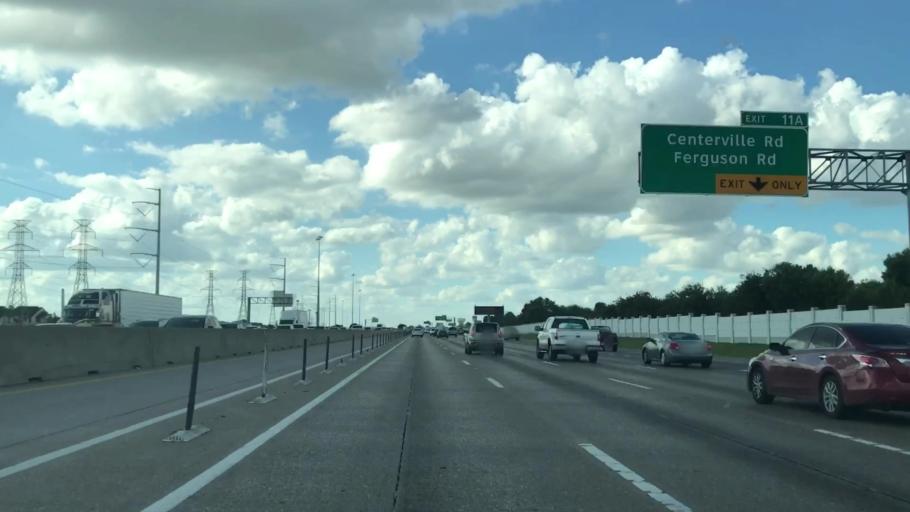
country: US
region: Texas
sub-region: Dallas County
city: Garland
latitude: 32.8494
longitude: -96.6398
